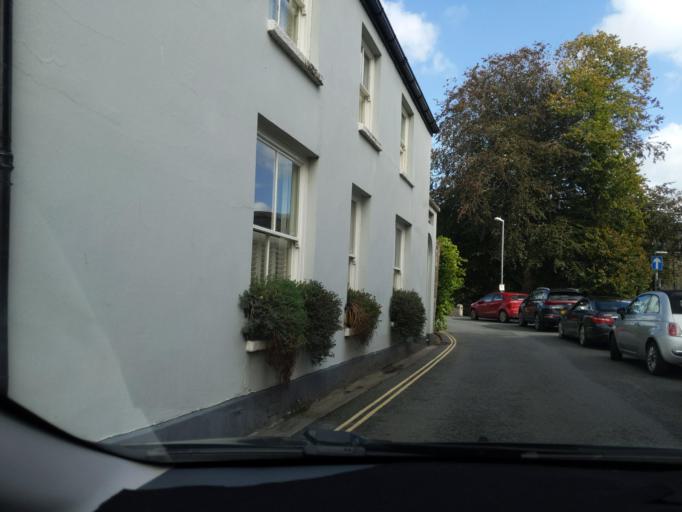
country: GB
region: England
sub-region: Cornwall
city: Lostwithiel
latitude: 50.4070
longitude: -4.6679
